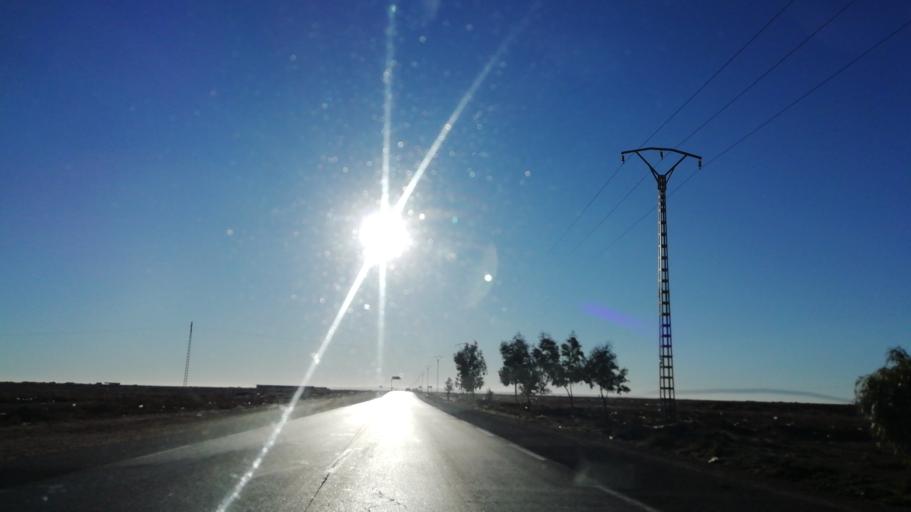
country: DZ
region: Saida
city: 'Ain el Hadjar
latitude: 34.0229
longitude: 0.1012
